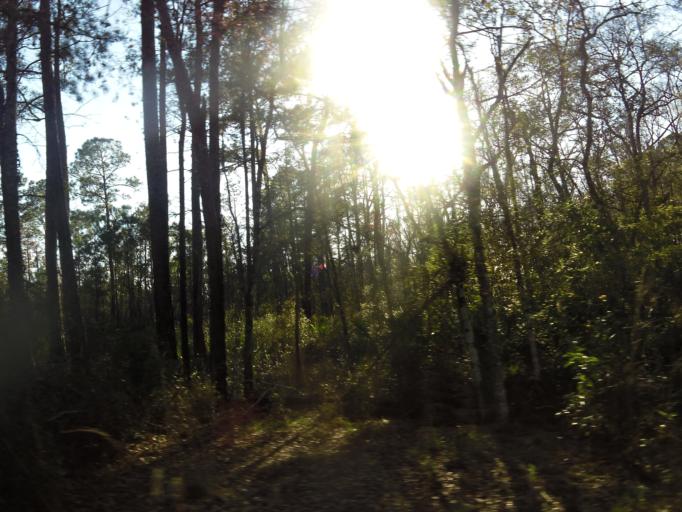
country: US
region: Florida
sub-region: Clay County
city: Middleburg
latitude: 30.1347
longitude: -81.9046
